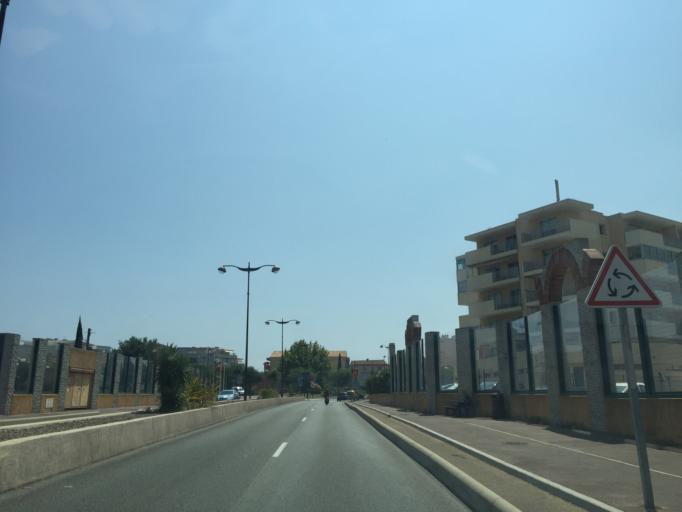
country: FR
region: Provence-Alpes-Cote d'Azur
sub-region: Departement du Var
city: Frejus
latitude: 43.4285
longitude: 6.7490
